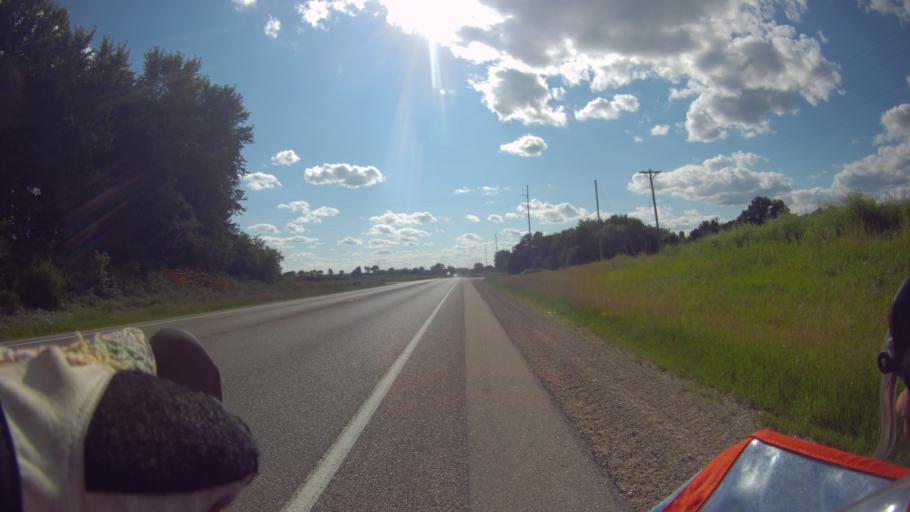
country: US
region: Wisconsin
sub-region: Dane County
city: Stoughton
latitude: 42.9190
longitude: -89.2842
